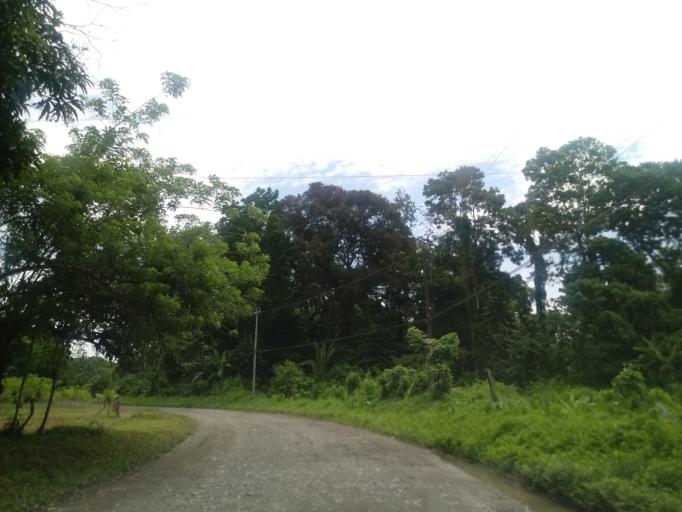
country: CR
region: Limon
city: Limon
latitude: 9.7488
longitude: -82.8824
